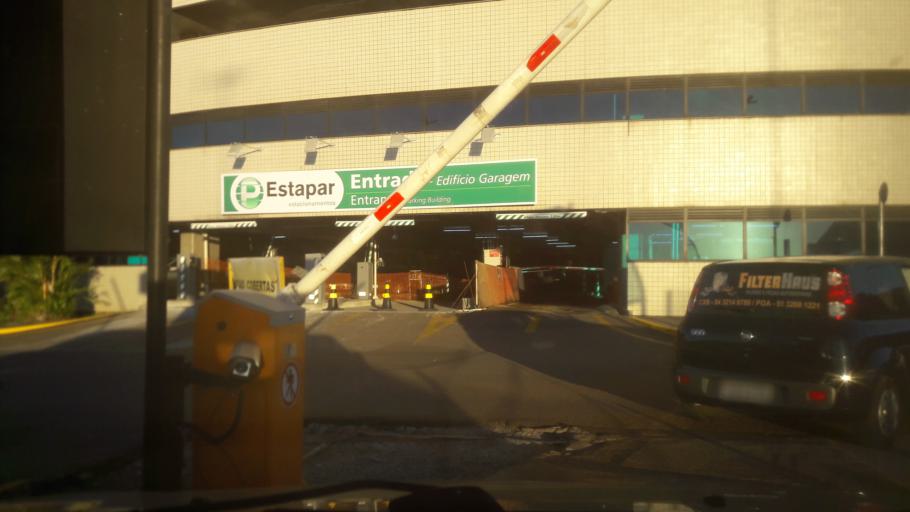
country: BR
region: Rio Grande do Sul
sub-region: Porto Alegre
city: Porto Alegre
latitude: -29.9892
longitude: -51.1768
